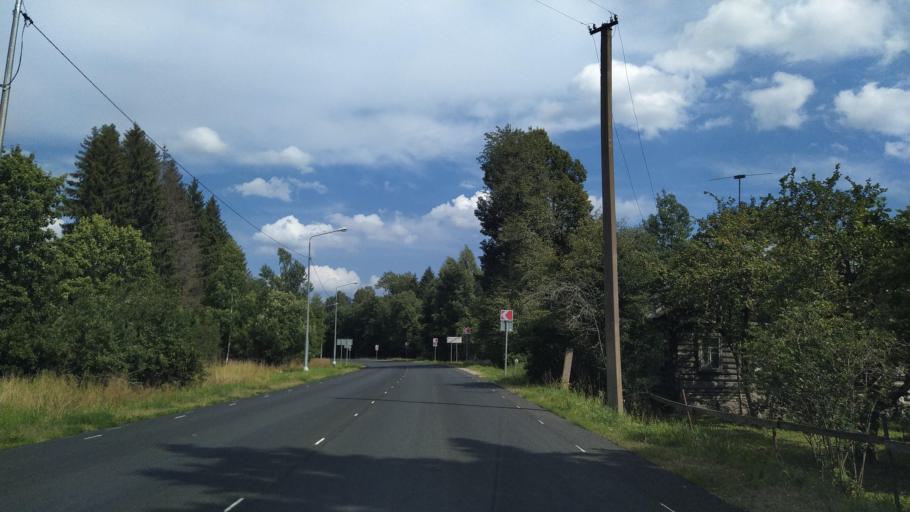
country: RU
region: Pskov
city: Vybor
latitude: 57.7101
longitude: 28.9102
